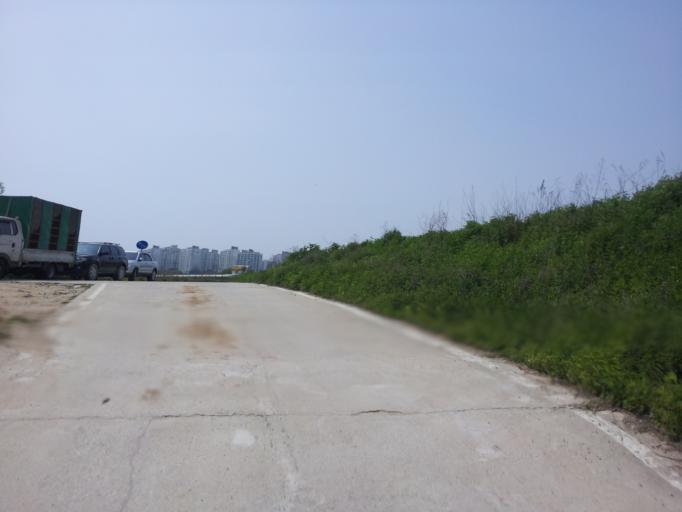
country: KR
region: Daejeon
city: Daejeon
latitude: 36.2662
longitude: 127.2806
